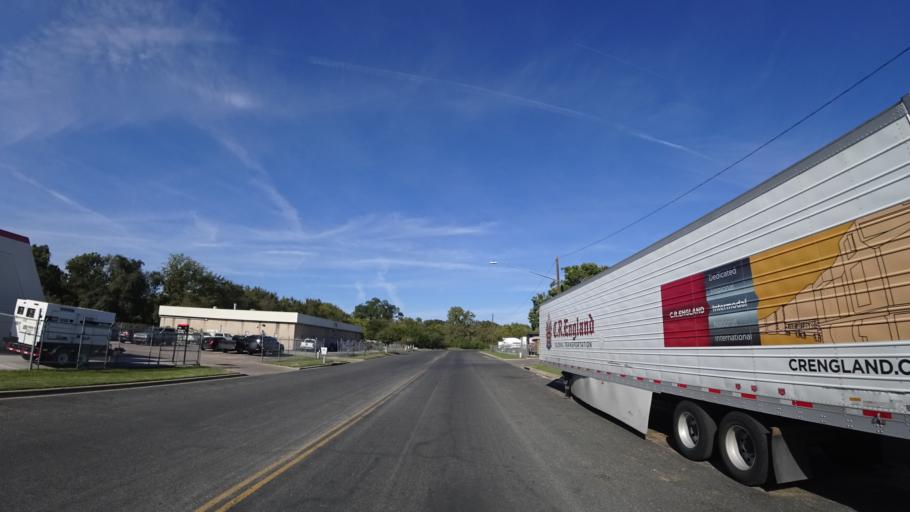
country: US
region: Texas
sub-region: Travis County
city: Austin
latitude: 30.2589
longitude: -97.6777
